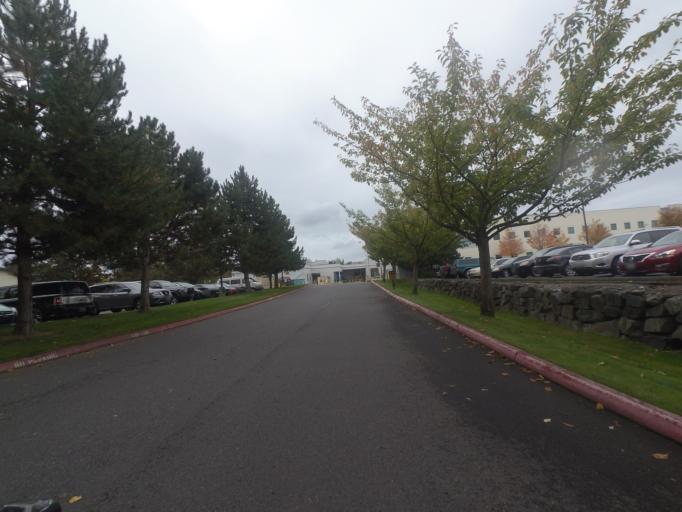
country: US
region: Washington
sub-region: Pierce County
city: McChord Air Force Base
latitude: 47.1544
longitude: -122.5000
